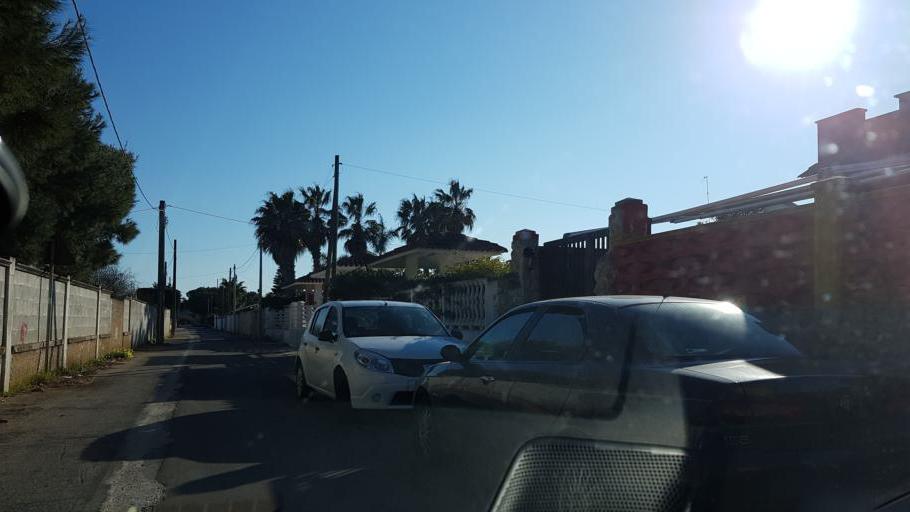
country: IT
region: Apulia
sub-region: Provincia di Brindisi
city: Materdomini
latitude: 40.6780
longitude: 17.9384
